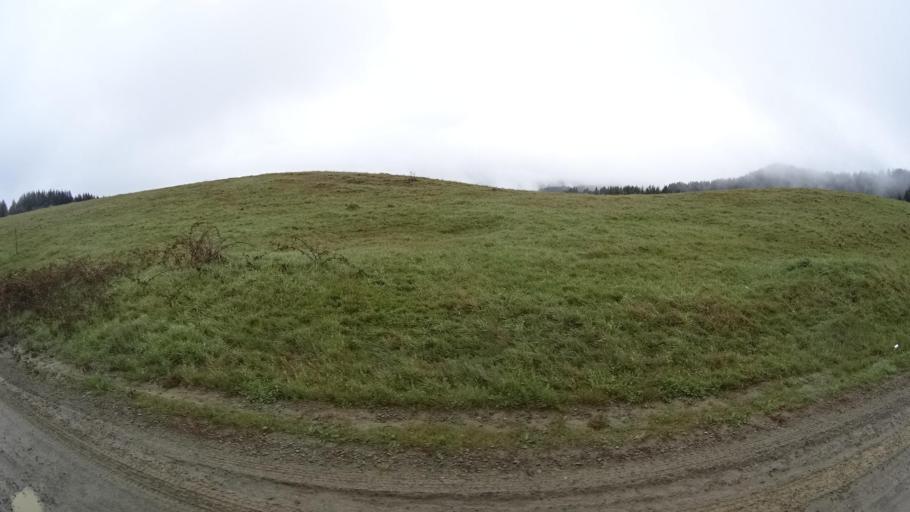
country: US
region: California
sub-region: Humboldt County
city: Westhaven-Moonstone
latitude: 41.1435
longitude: -123.8662
